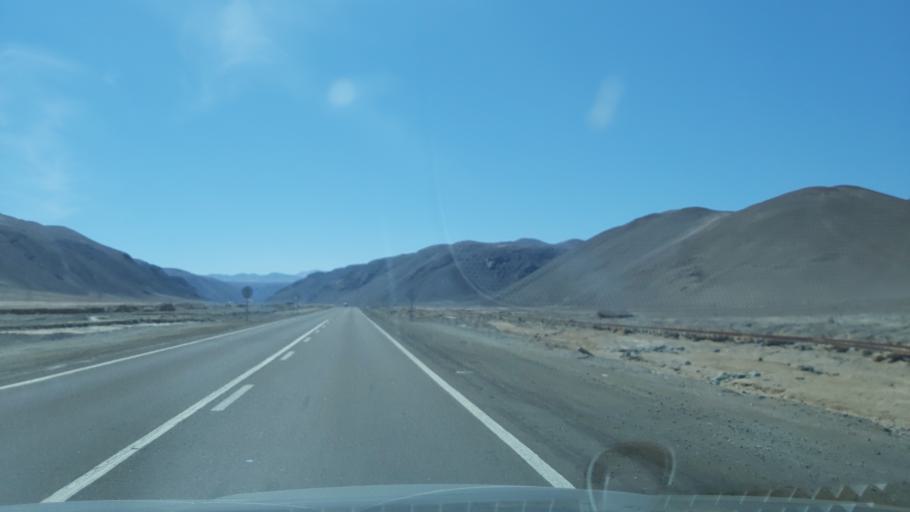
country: CL
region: Atacama
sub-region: Provincia de Chanaral
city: Diego de Almagro
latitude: -26.3486
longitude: -69.8619
